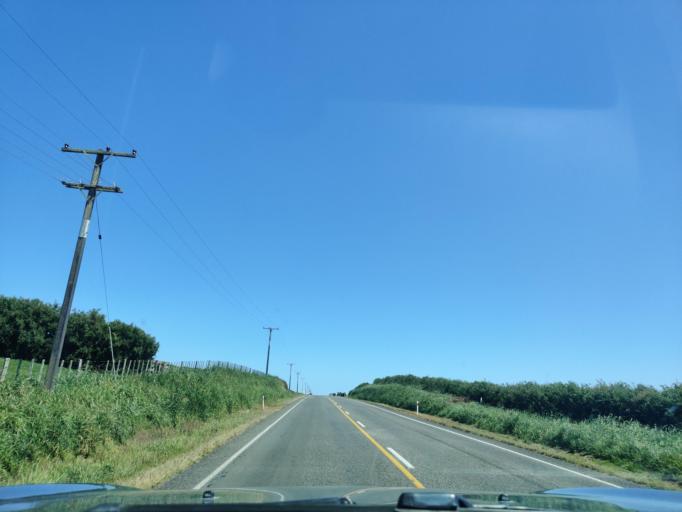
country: NZ
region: Taranaki
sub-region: South Taranaki District
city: Patea
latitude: -39.7464
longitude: 174.5226
